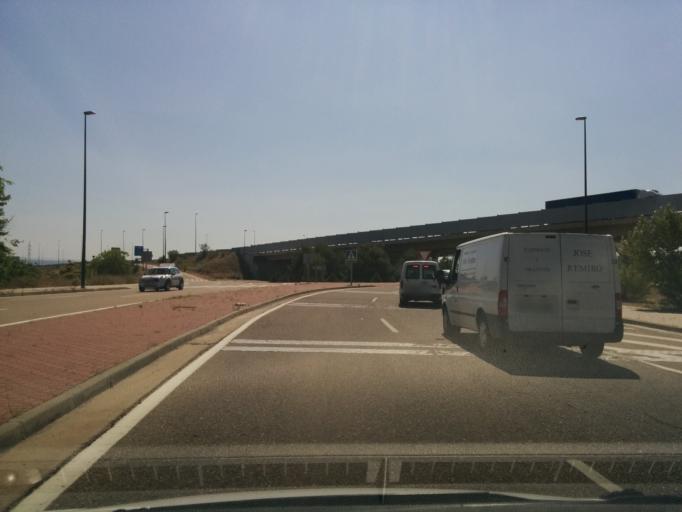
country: ES
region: Aragon
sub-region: Provincia de Zaragoza
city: Zaragoza
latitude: 41.6215
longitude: -0.8627
